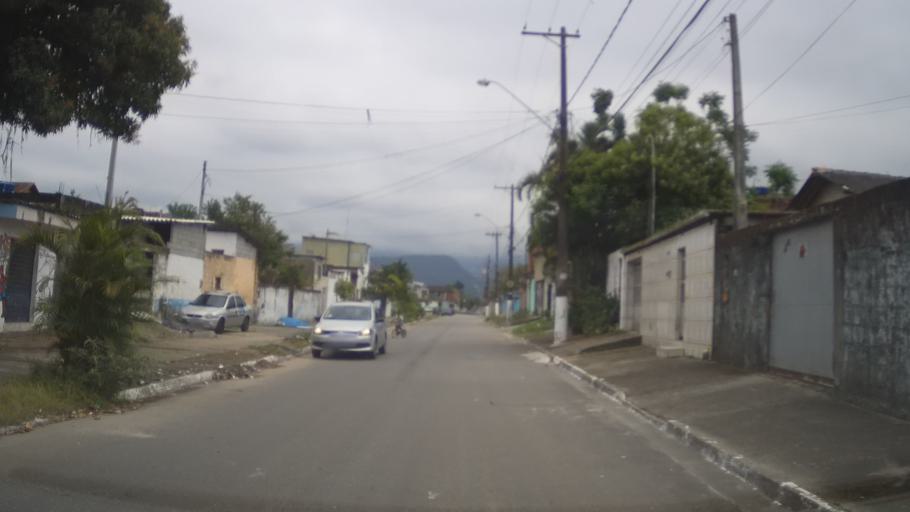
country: BR
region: Sao Paulo
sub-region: Praia Grande
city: Praia Grande
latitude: -24.0221
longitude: -46.4948
